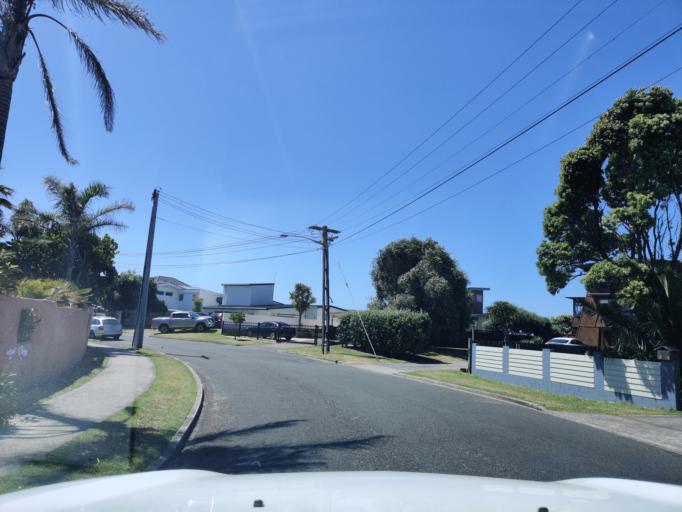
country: NZ
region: Bay of Plenty
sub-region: Western Bay of Plenty District
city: Maketu
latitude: -37.7156
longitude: 176.3394
